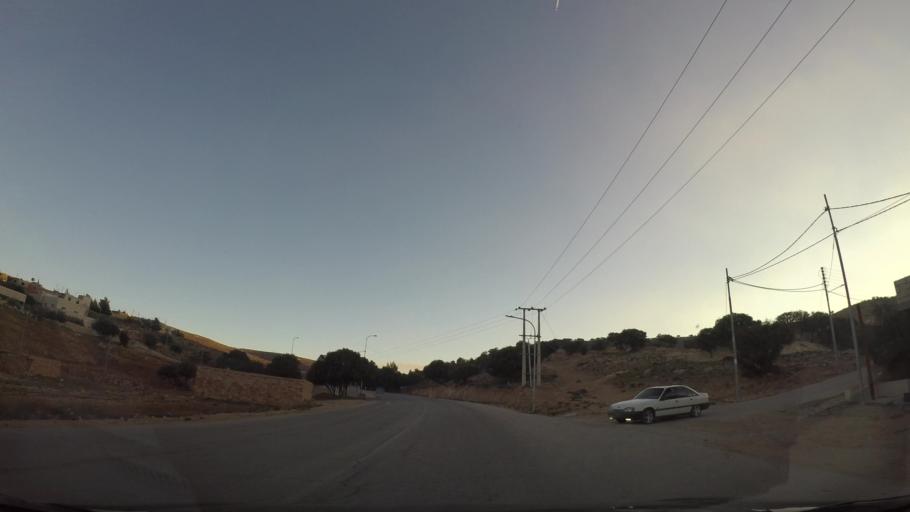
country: JO
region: Ma'an
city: Petra
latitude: 30.4153
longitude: 35.5082
